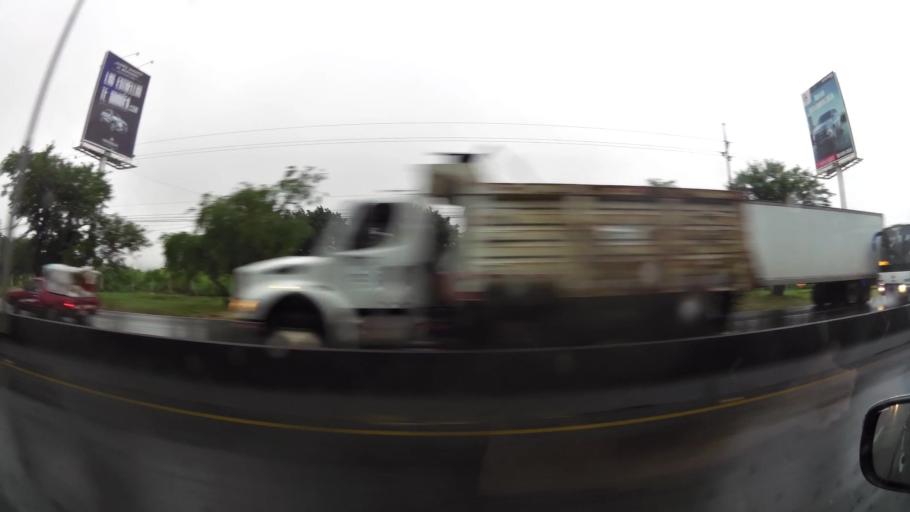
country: CR
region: Heredia
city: Llorente
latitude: 9.9989
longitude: -84.1704
